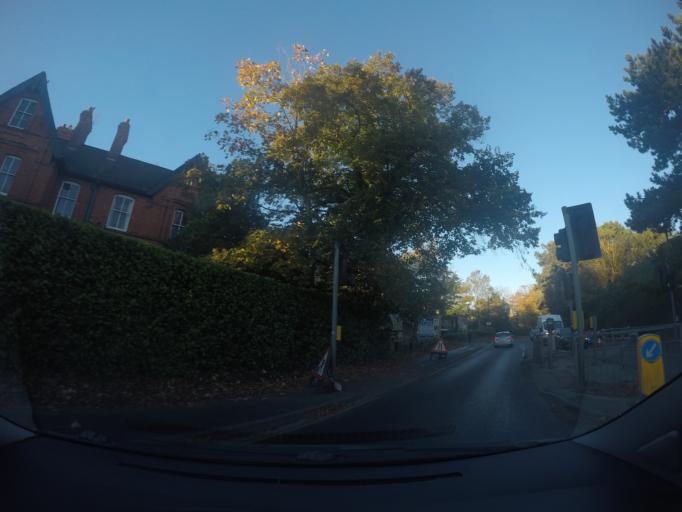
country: GB
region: England
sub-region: City of York
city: York
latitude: 53.9712
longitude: -1.0992
